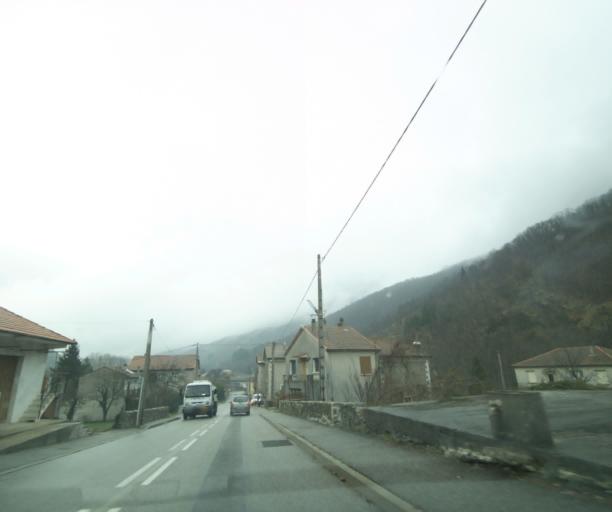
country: FR
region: Rhone-Alpes
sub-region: Departement de l'Ardeche
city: Thueyts
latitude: 44.6669
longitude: 4.1096
